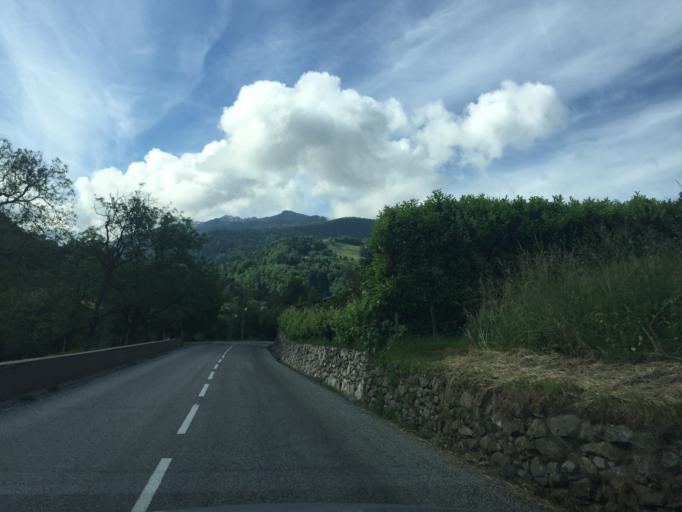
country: FR
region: Rhone-Alpes
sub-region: Departement de la Savoie
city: La Rochette
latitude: 45.4452
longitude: 6.1215
